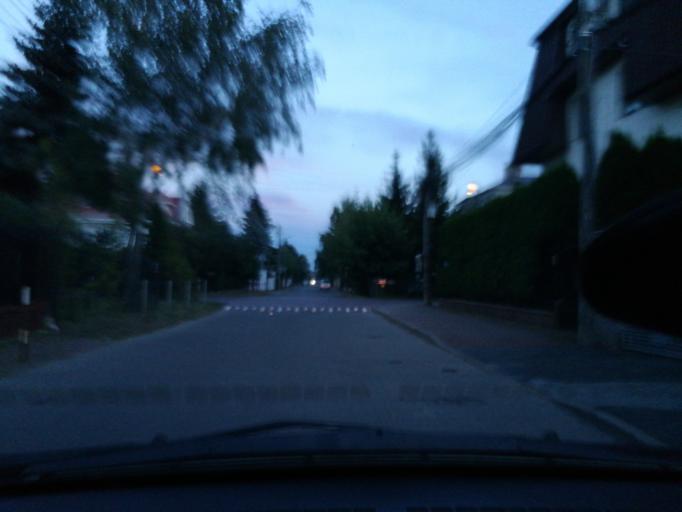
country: PL
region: Masovian Voivodeship
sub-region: Warszawa
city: Wilanow
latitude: 52.1749
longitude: 21.0731
